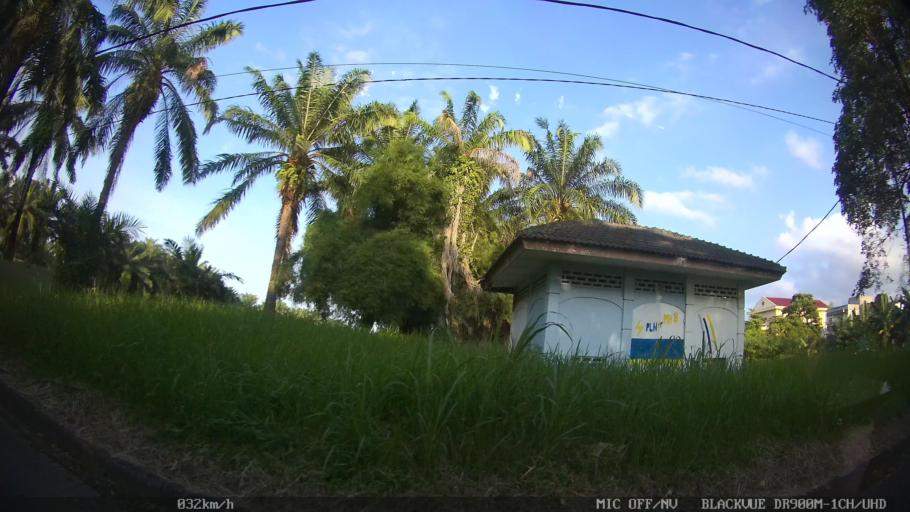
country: ID
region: North Sumatra
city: Medan
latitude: 3.6213
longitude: 98.6537
